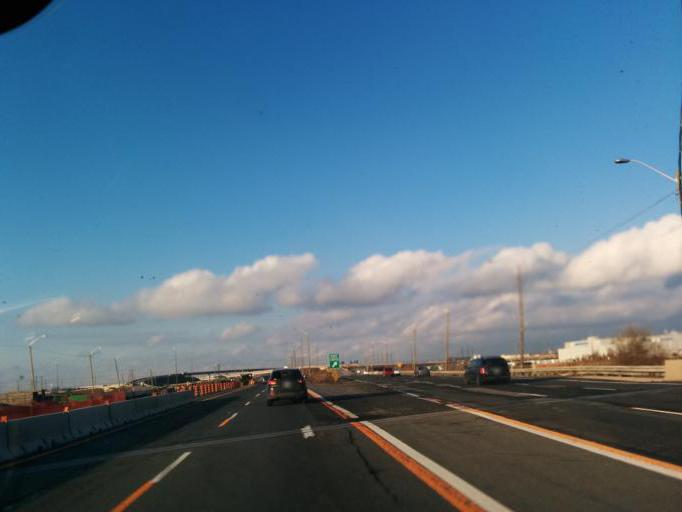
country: CA
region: Ontario
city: Etobicoke
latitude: 43.7459
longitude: -79.6295
